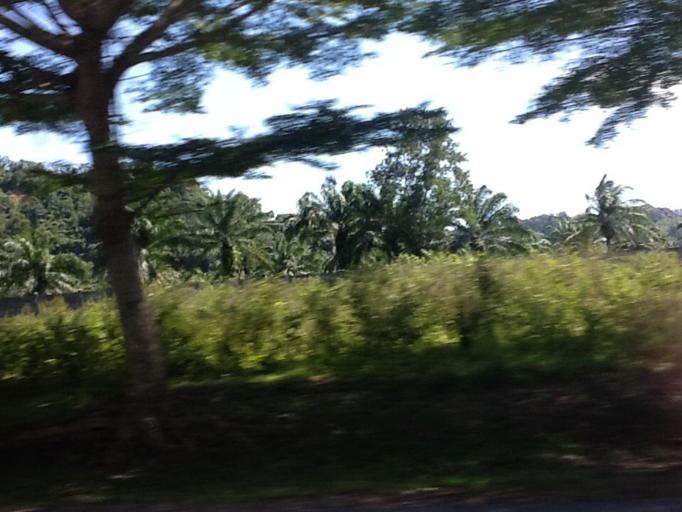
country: TH
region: Phuket
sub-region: Amphoe Kathu
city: Kathu
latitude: 7.9354
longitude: 98.3336
